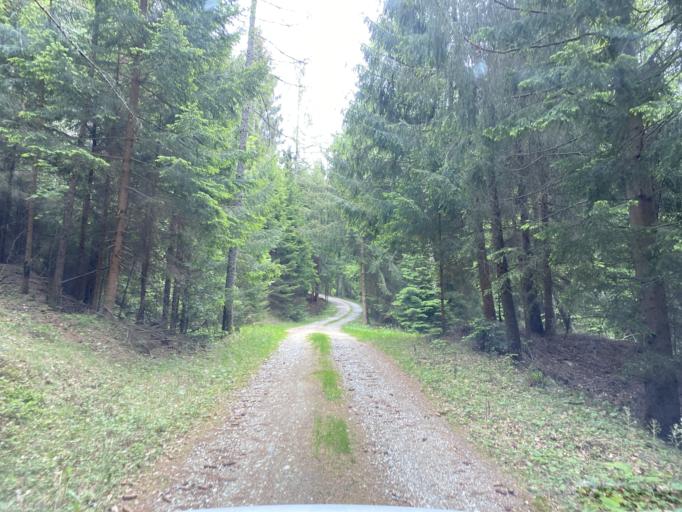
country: AT
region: Styria
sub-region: Politischer Bezirk Weiz
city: Koglhof
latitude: 47.3083
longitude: 15.7043
